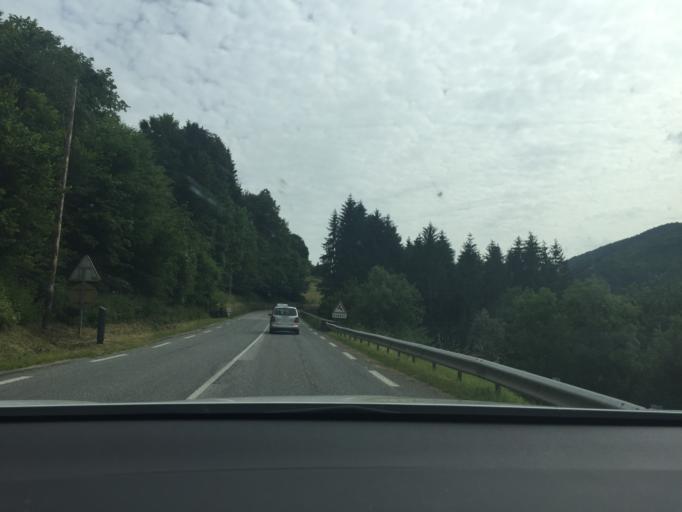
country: FR
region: Rhone-Alpes
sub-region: Departement de la Savoie
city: Vimines
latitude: 45.4979
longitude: 5.8394
